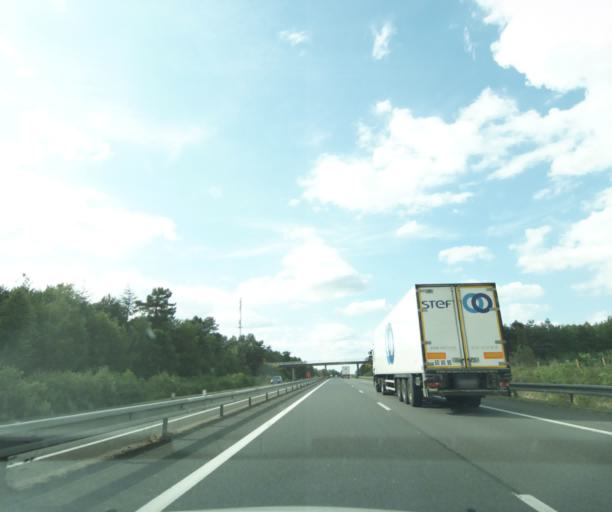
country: FR
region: Centre
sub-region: Departement du Loir-et-Cher
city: Chaumont-sur-Tharonne
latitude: 47.6405
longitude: 1.9474
